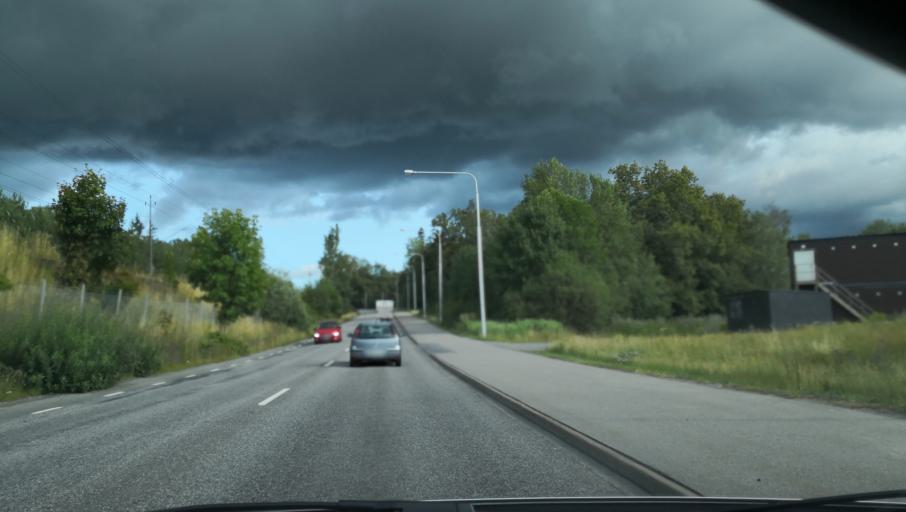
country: SE
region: Stockholm
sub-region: Stockholms Kommun
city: Arsta
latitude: 59.2469
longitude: 18.0665
